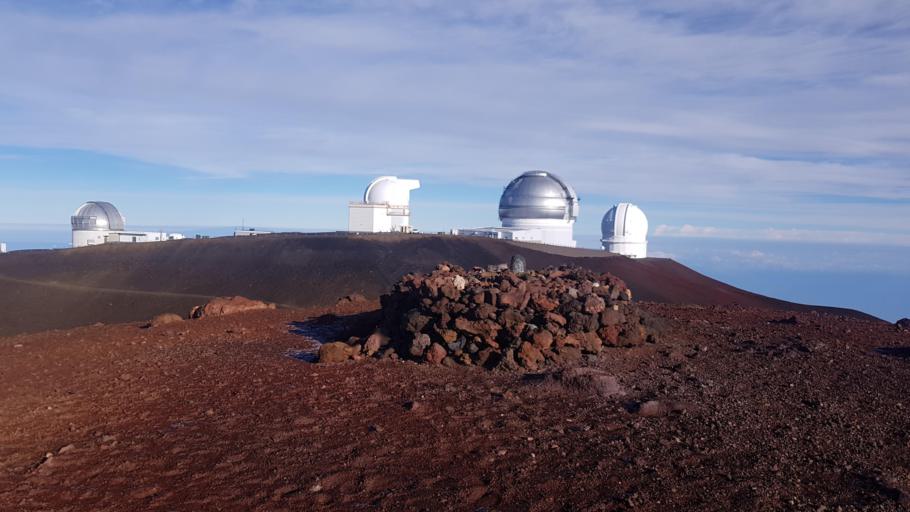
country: US
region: Hawaii
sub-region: Hawaii County
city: Honoka'a
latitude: 19.8204
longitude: -155.4678
